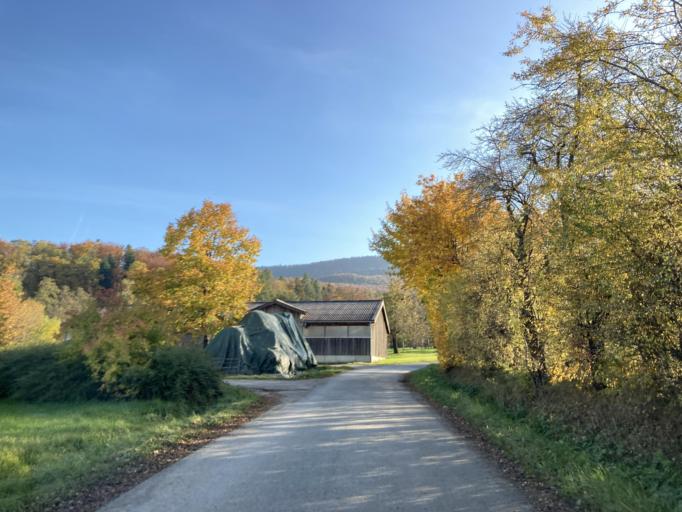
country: DE
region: Baden-Wuerttemberg
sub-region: Tuebingen Region
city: Mossingen
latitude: 48.3904
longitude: 9.0415
